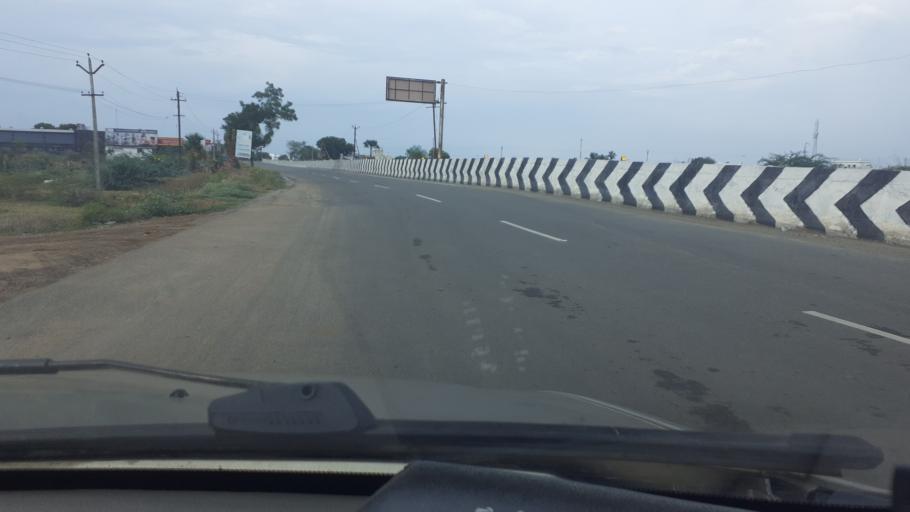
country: IN
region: Tamil Nadu
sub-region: Tirunelveli Kattabo
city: Tirunelveli
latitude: 8.6599
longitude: 77.7146
